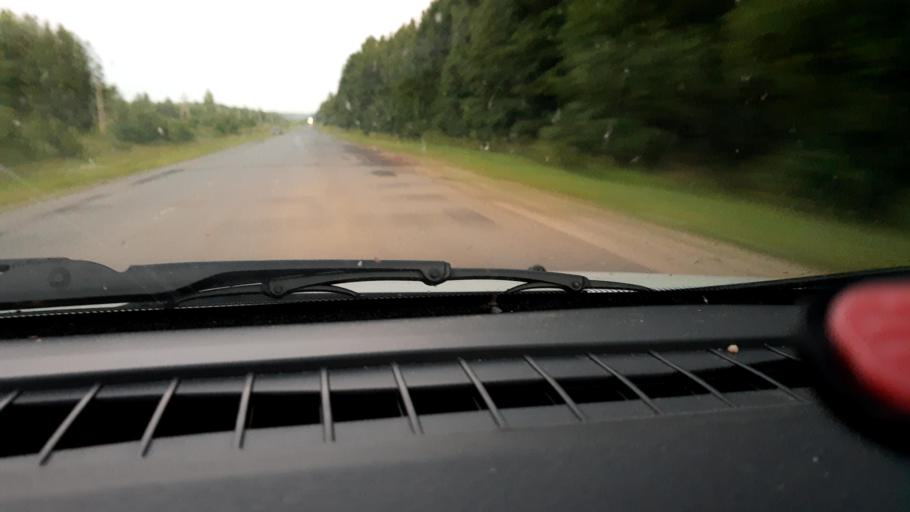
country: RU
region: Nizjnij Novgorod
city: Uren'
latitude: 57.4765
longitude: 46.0377
